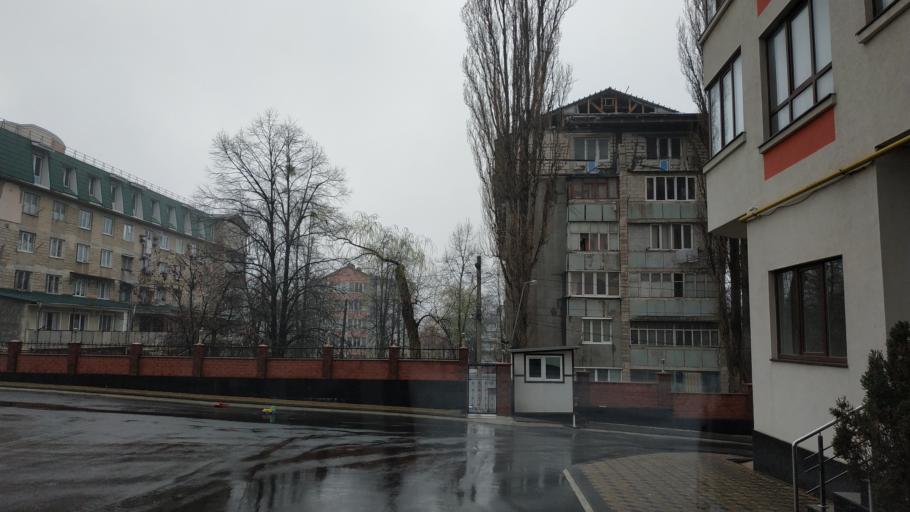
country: MD
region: Chisinau
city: Vatra
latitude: 47.0347
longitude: 28.7794
